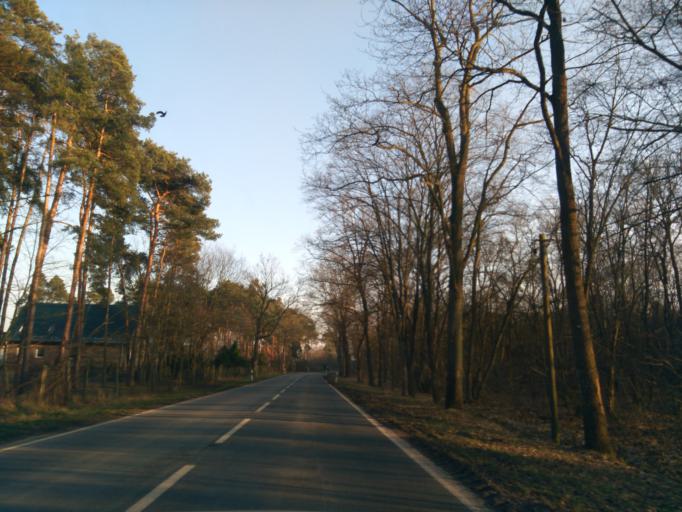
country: DE
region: Brandenburg
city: Brieselang
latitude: 52.6077
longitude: 13.0293
